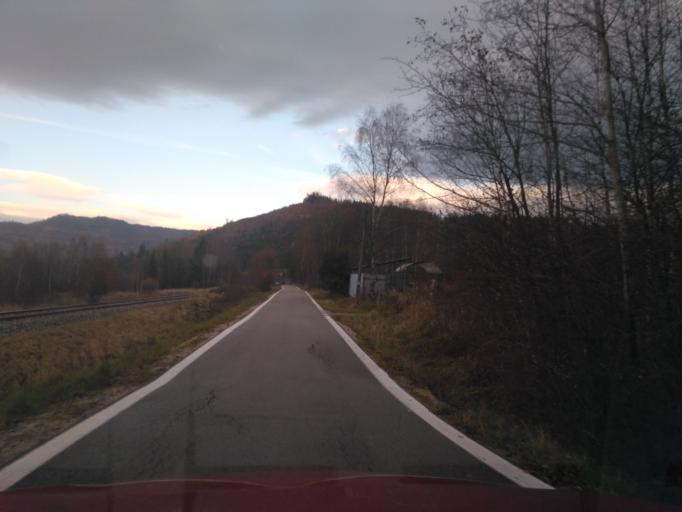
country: SK
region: Kosicky
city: Spisska Nova Ves
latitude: 48.8205
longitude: 20.5949
